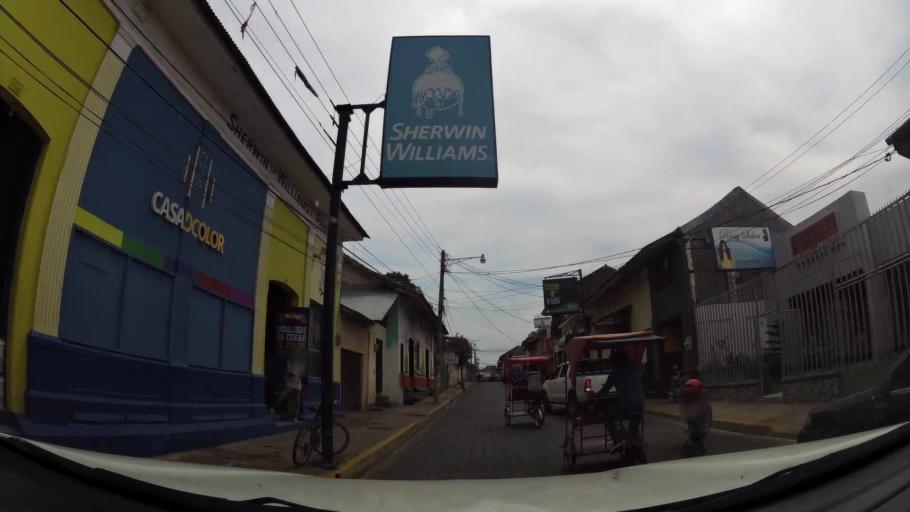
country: NI
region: Rivas
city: Rivas
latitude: 11.4405
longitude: -85.8281
